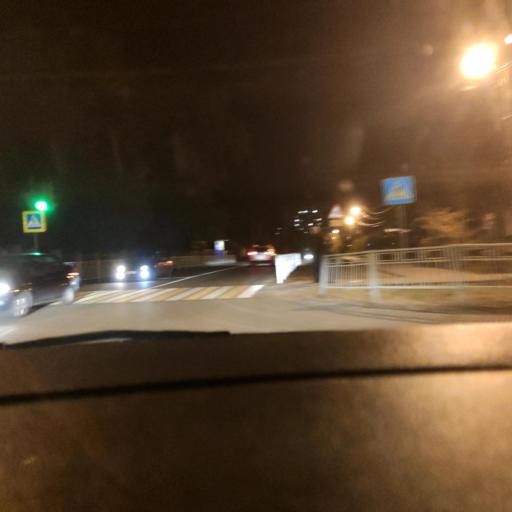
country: RU
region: Voronezj
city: Voronezh
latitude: 51.6955
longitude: 39.1899
